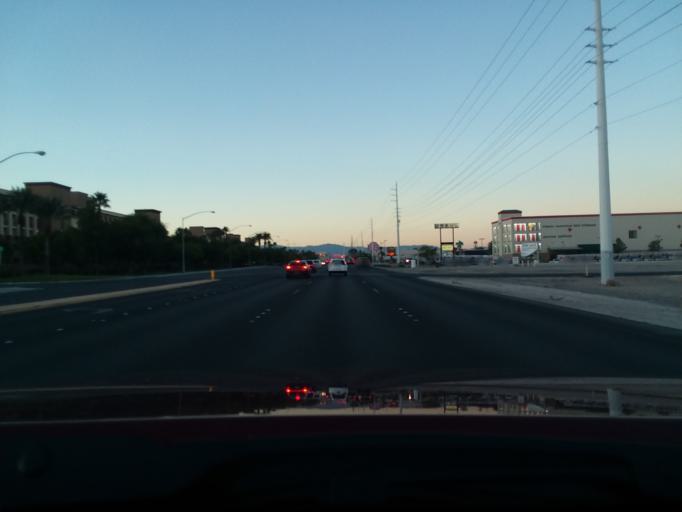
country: US
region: Nevada
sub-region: Clark County
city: Enterprise
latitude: 36.0313
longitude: -115.1723
